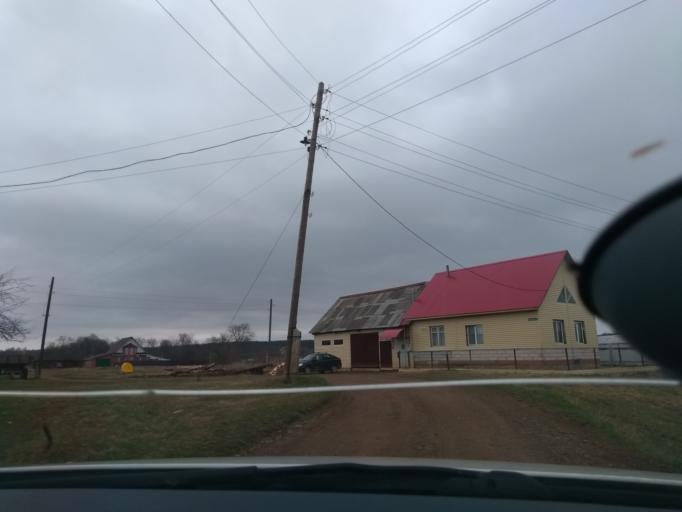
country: RU
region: Perm
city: Orda
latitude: 57.2236
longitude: 56.5989
